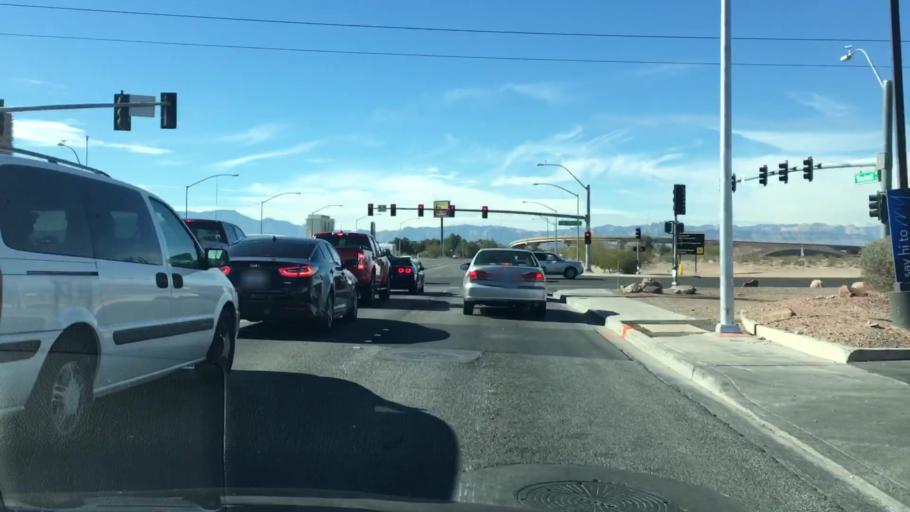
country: US
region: Nevada
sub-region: Clark County
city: Paradise
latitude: 36.0424
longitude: -115.1717
